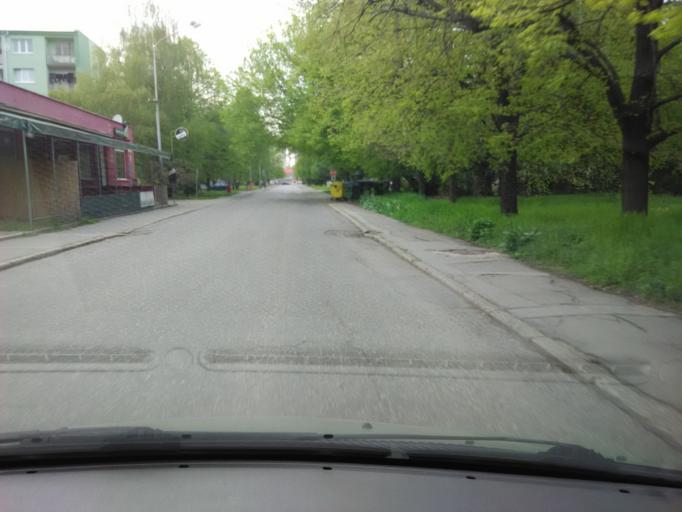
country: SK
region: Nitriansky
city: Levice
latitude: 48.2123
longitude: 18.6023
